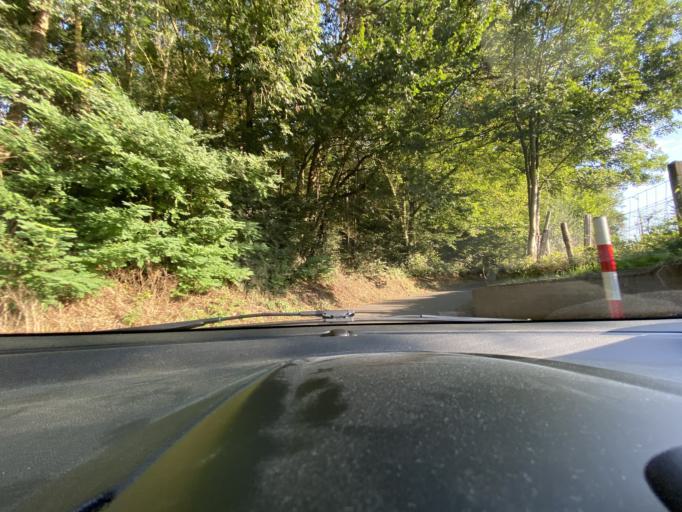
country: NL
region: Limburg
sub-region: Gemeente Meerssen
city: Meerssen
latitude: 50.8935
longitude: 5.7613
